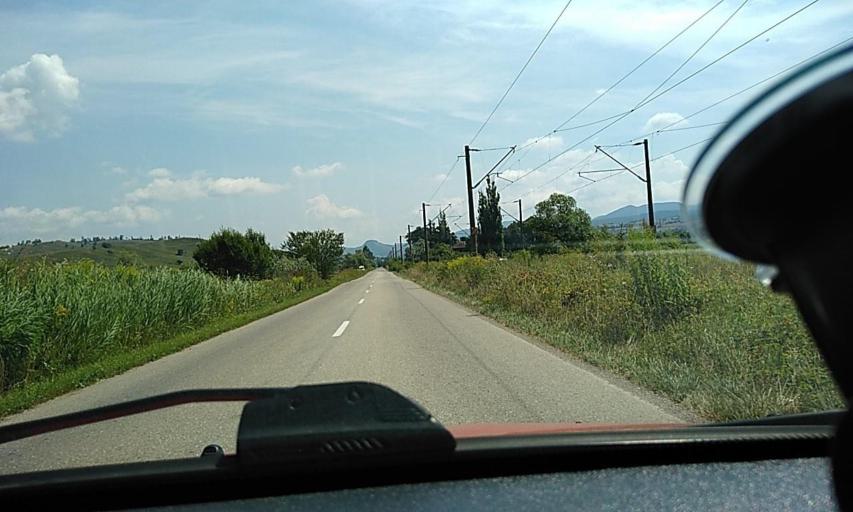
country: RO
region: Brasov
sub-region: Comuna Hoghiz
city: Hoghiz
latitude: 46.0291
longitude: 25.3694
